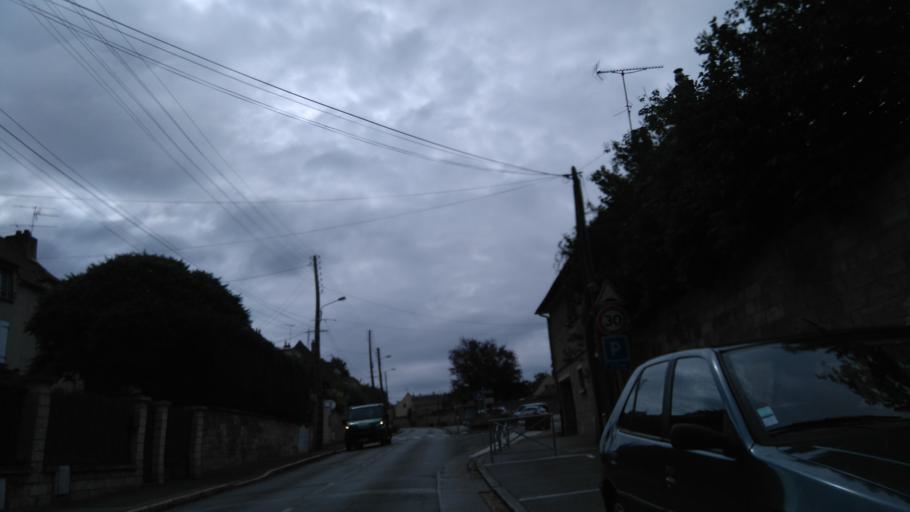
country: FR
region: Picardie
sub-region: Departement de l'Oise
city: Saint-Maximin
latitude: 49.2221
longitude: 2.4446
